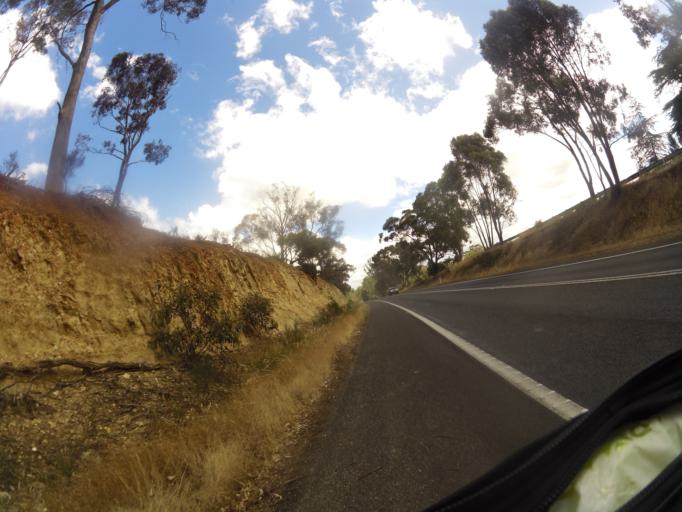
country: AU
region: Victoria
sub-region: Mount Alexander
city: Castlemaine
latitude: -37.0380
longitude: 144.2273
